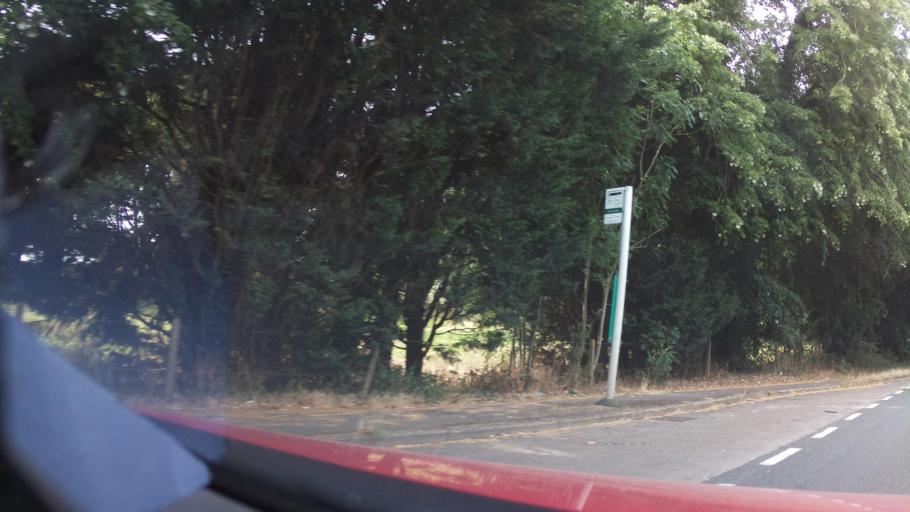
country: GB
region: England
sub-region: Surrey
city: Dorking
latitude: 51.2389
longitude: -0.3031
